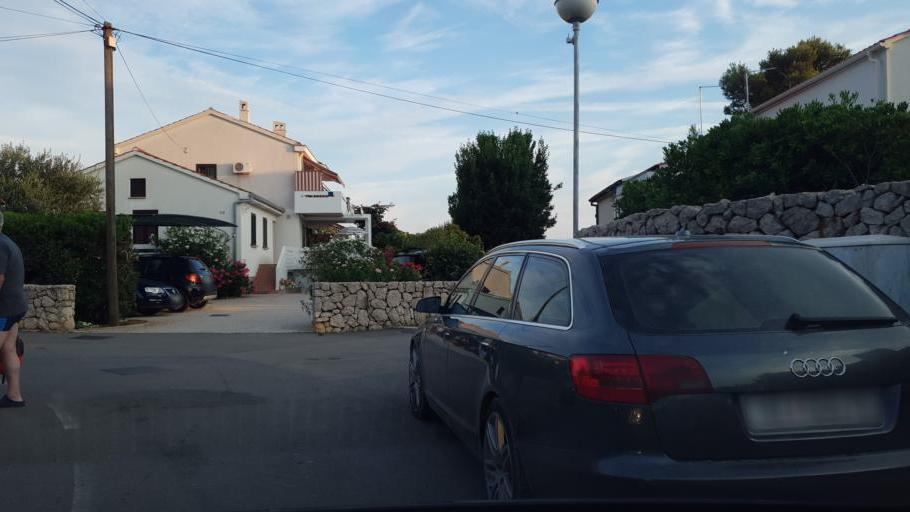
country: HR
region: Primorsko-Goranska
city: Punat
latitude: 45.0108
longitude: 14.6241
